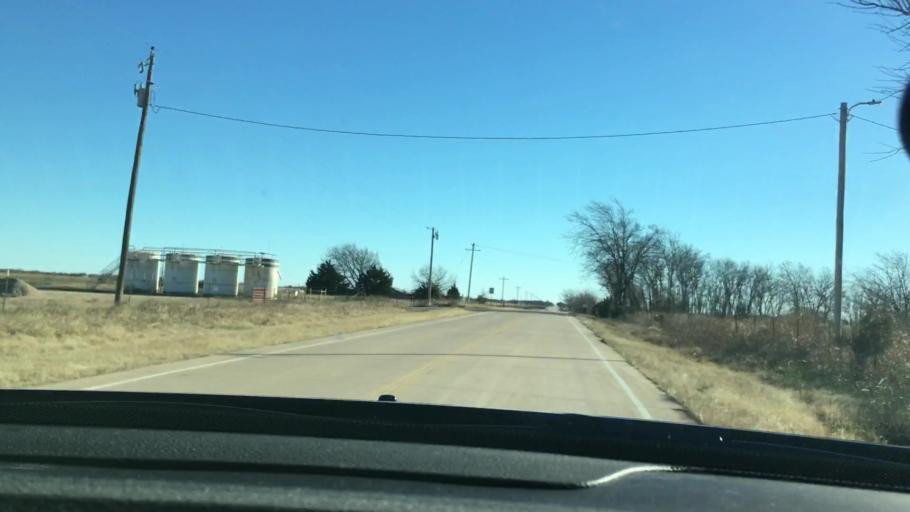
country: US
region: Oklahoma
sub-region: Marshall County
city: Madill
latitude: 34.1144
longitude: -96.7076
